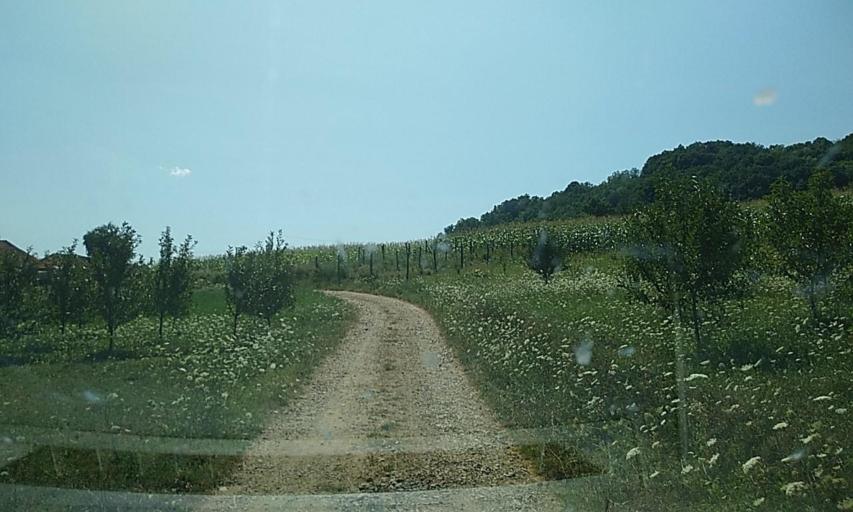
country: RS
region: Central Serbia
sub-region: Pcinjski Okrug
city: Vladicin Han
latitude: 42.7609
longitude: 22.0748
